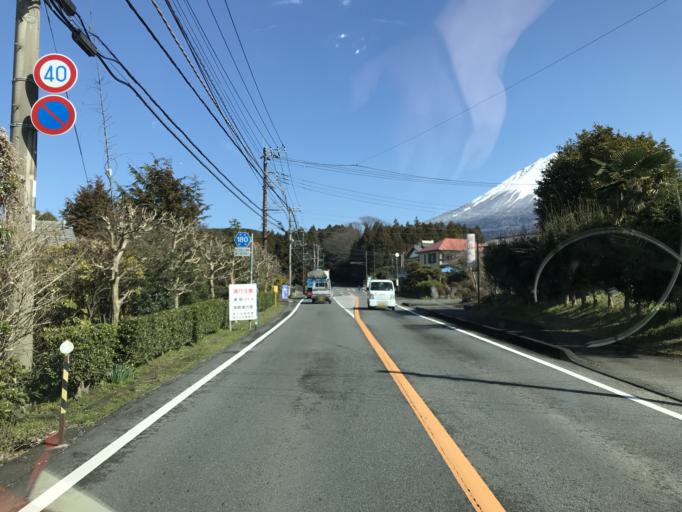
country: JP
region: Shizuoka
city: Fujinomiya
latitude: 35.2635
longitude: 138.6335
